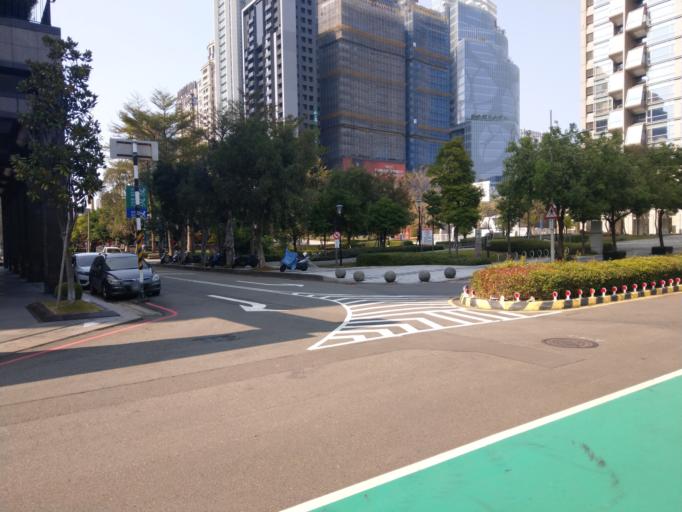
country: TW
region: Taiwan
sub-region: Taichung City
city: Taichung
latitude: 24.1598
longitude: 120.6451
